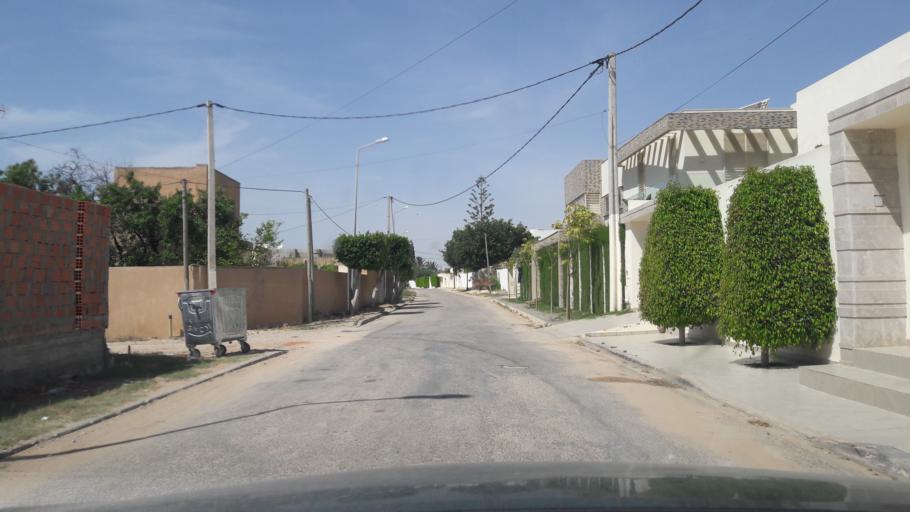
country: TN
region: Safaqis
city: Al Qarmadah
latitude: 34.7891
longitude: 10.7565
